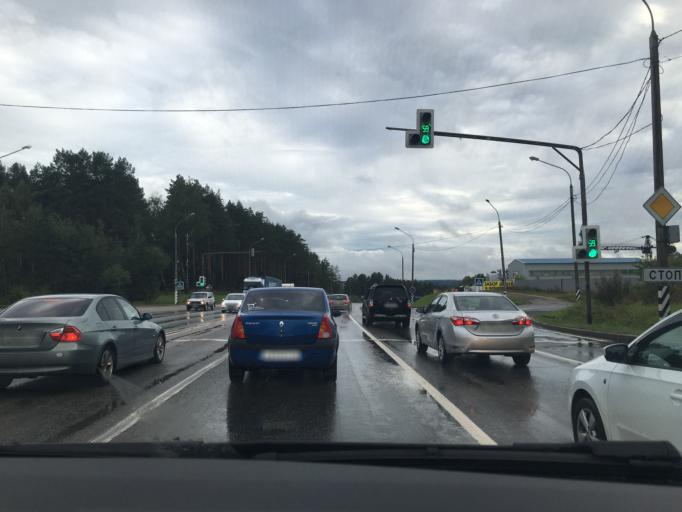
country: RU
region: Kaluga
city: Obninsk
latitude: 55.0578
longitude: 36.6193
